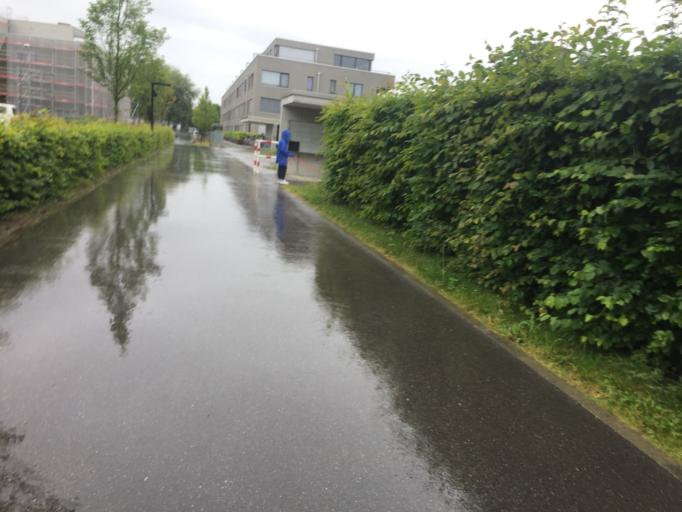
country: CH
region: Bern
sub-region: Bern-Mittelland District
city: Munsingen
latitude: 46.8702
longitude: 7.5543
